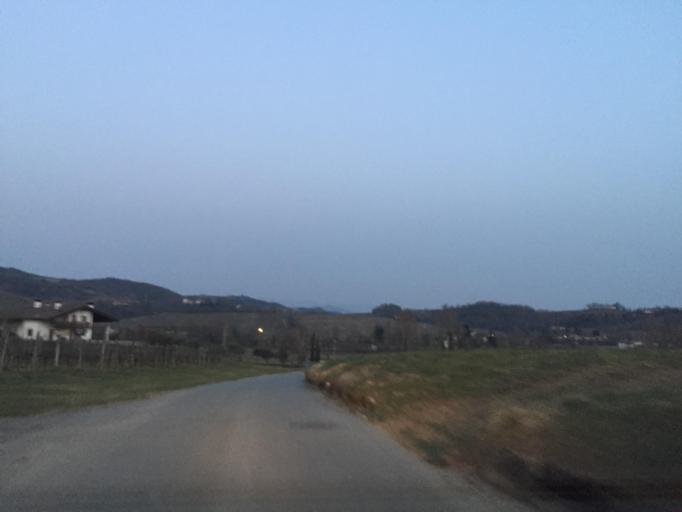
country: IT
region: Friuli Venezia Giulia
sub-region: Provincia di Gorizia
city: Dolegna del Collio
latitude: 46.0245
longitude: 13.4698
